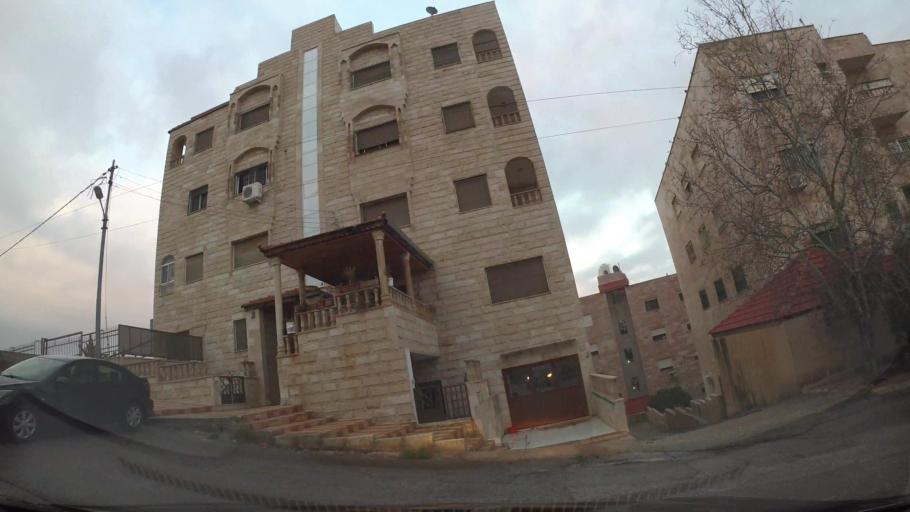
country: JO
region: Amman
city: Amman
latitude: 31.9832
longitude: 35.9141
